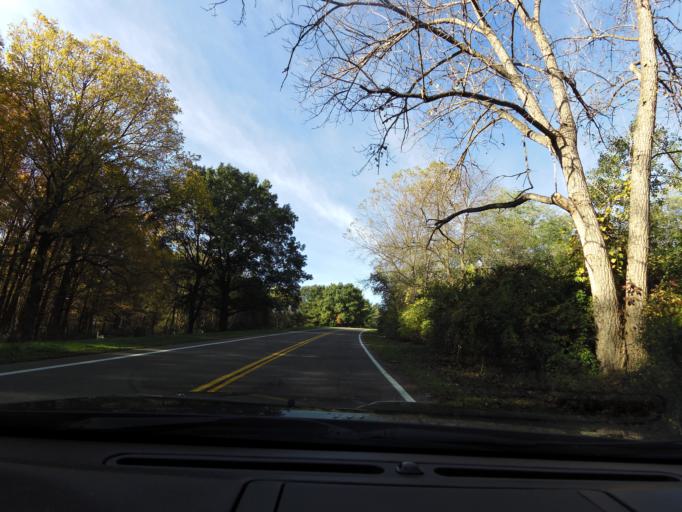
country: US
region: New York
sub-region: Livingston County
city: Mount Morris
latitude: 42.7386
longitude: -77.8938
